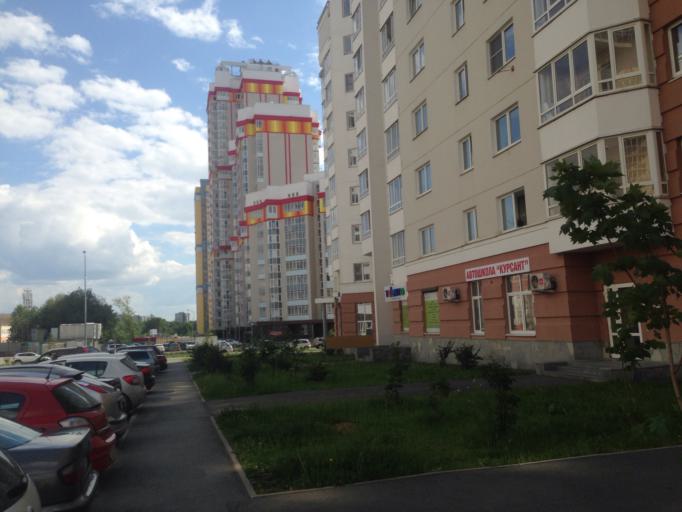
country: RU
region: Sverdlovsk
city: Yekaterinburg
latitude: 56.8061
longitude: 60.6052
